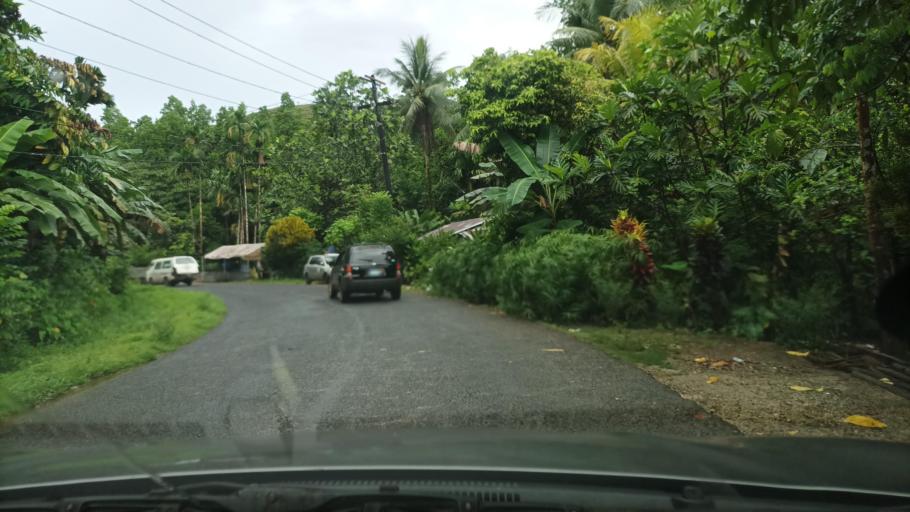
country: FM
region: Pohnpei
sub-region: Sokehs Municipality
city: Palikir - National Government Center
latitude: 6.8518
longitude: 158.1611
